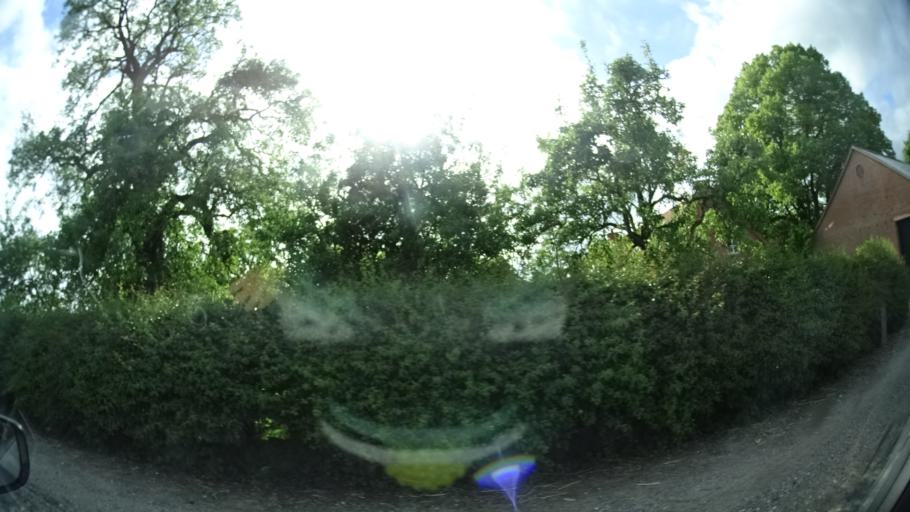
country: DK
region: Central Jutland
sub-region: Syddjurs Kommune
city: Ronde
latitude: 56.3312
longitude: 10.4352
